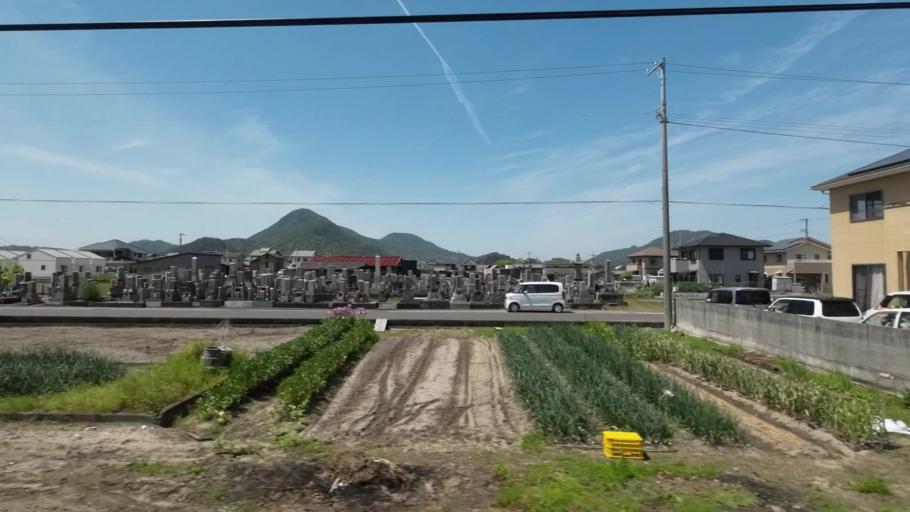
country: JP
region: Kagawa
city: Marugame
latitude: 34.2401
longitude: 133.7830
